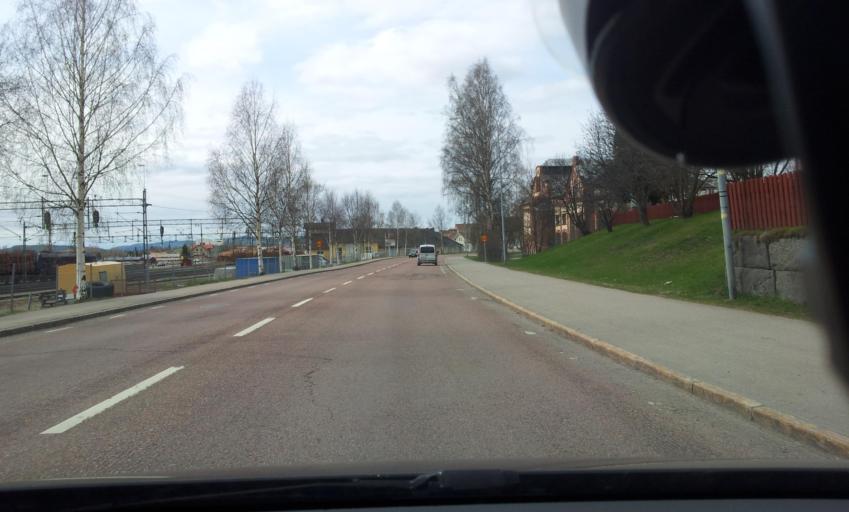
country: SE
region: Gaevleborg
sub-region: Ljusdals Kommun
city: Ljusdal
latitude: 61.8243
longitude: 16.1063
